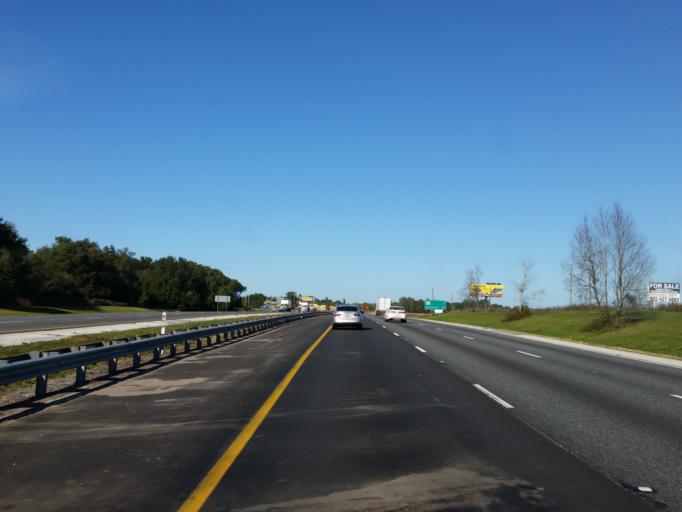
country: US
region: Florida
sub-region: Marion County
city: Ocala
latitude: 29.2202
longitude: -82.1844
